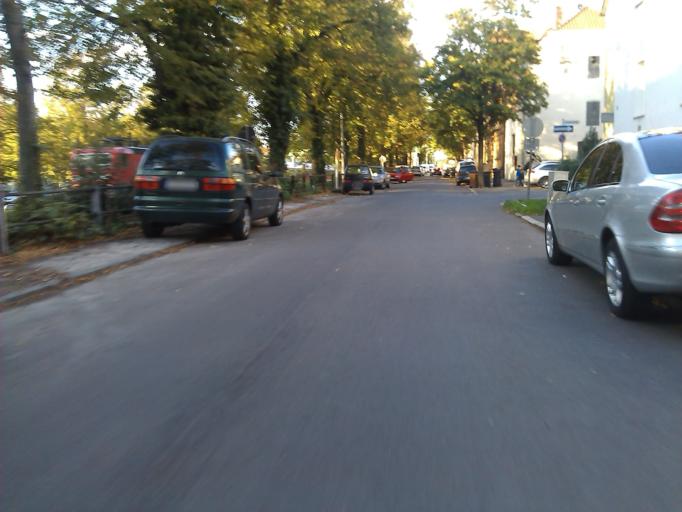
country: DE
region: Baden-Wuerttemberg
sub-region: Regierungsbezirk Stuttgart
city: Heilbronn
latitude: 49.1527
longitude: 9.2213
